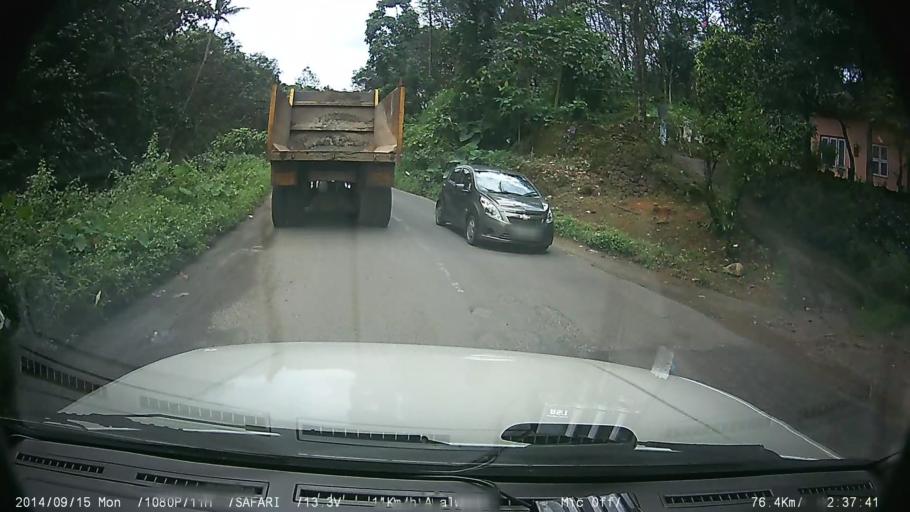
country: IN
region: Kerala
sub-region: Ernakulam
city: Muvattupuzha
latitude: 9.8963
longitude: 76.5868
